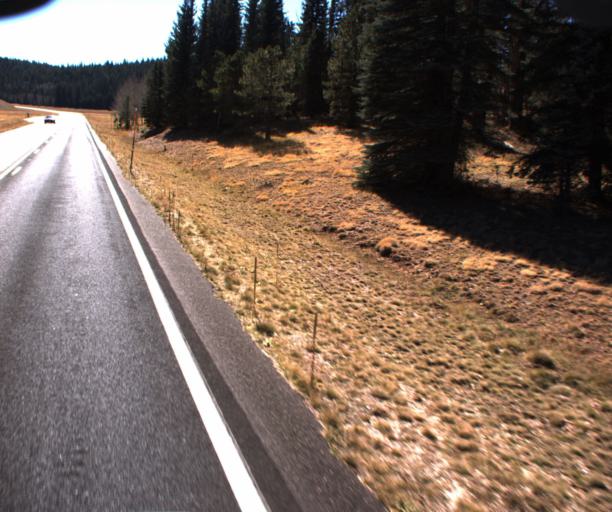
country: US
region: Arizona
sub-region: Coconino County
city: Grand Canyon
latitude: 36.5327
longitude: -112.1517
